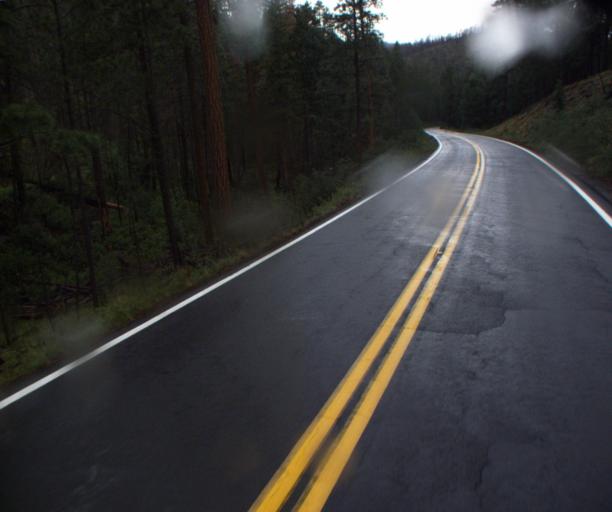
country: US
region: Arizona
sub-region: Apache County
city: Eagar
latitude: 33.7331
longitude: -109.2041
